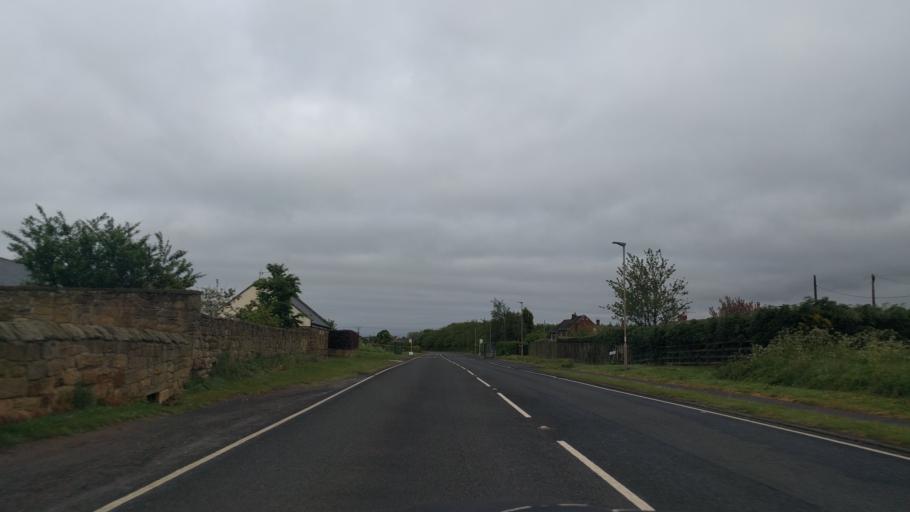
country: GB
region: England
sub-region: Northumberland
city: Choppington
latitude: 55.1613
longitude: -1.6261
